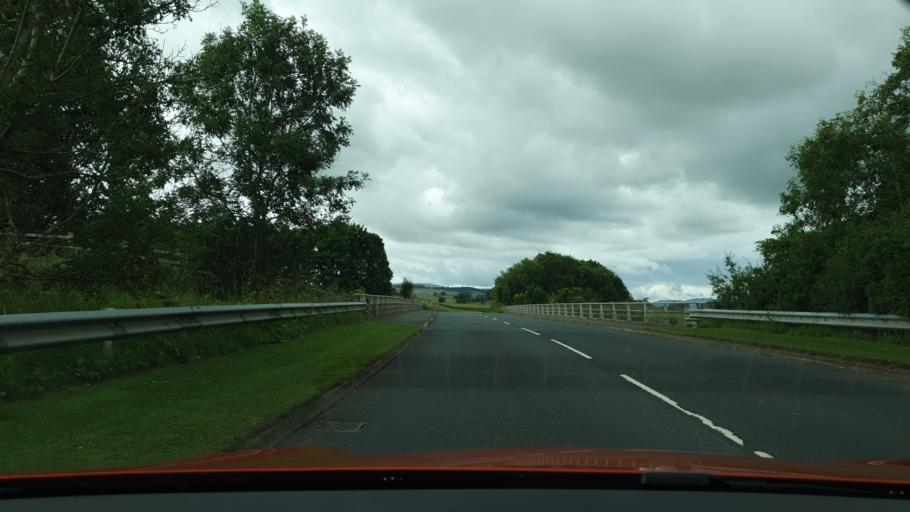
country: GB
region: England
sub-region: Cumbria
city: Penrith
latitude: 54.6473
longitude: -2.7445
